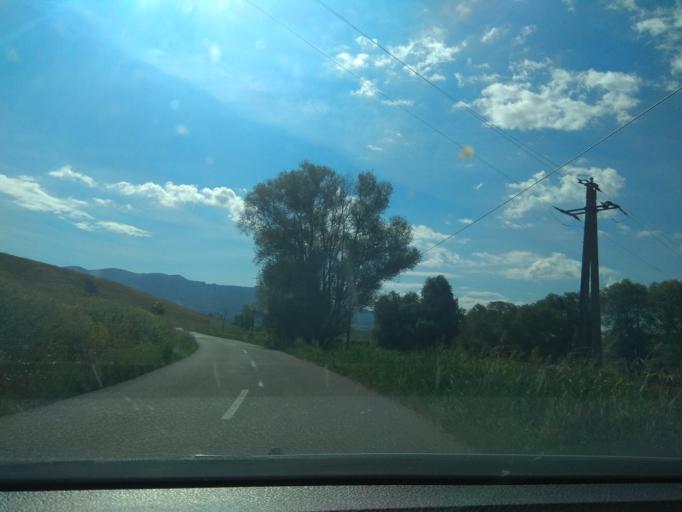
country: HU
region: Borsod-Abauj-Zemplen
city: Borsodnadasd
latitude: 48.0731
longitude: 20.3008
